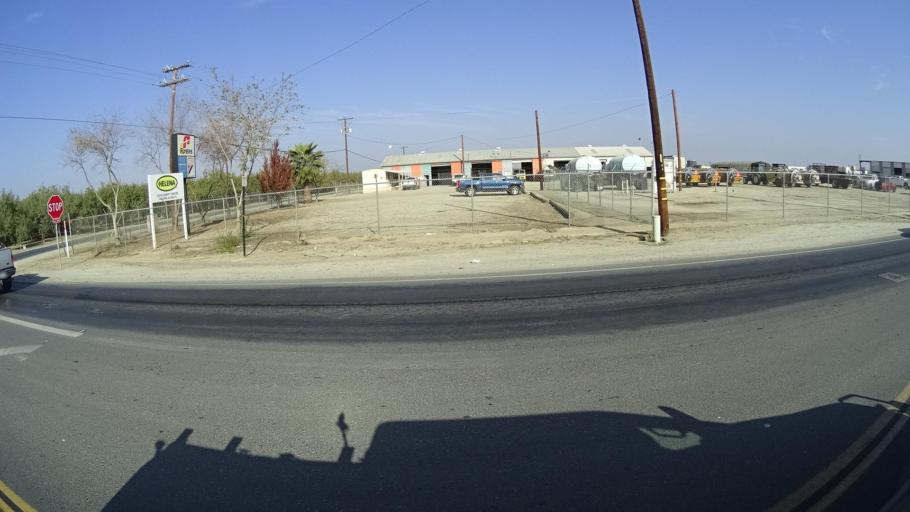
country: US
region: California
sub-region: Kern County
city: Delano
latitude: 35.7902
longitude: -119.2323
